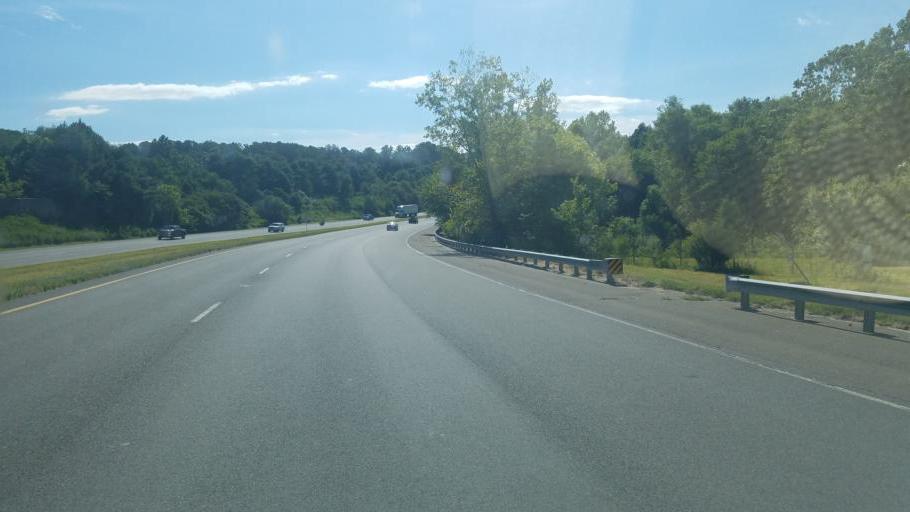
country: US
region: Virginia
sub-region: Fauquier County
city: Warrenton
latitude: 38.7375
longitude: -77.8022
